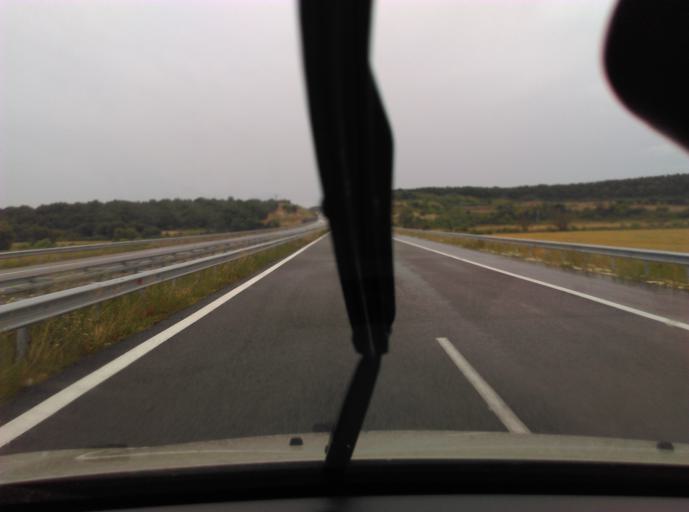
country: BG
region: Khaskovo
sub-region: Obshtina Dimitrovgrad
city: Dimitrovgrad
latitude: 42.0326
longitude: 25.5475
